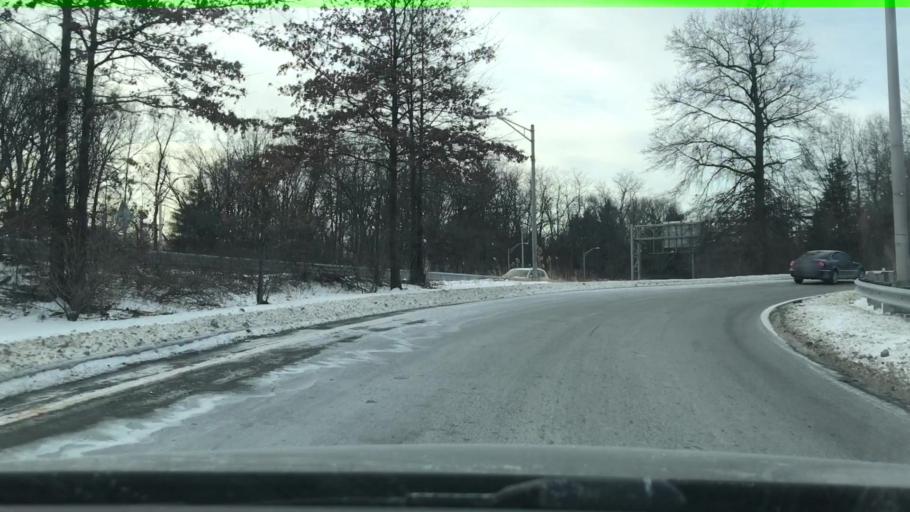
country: US
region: New Jersey
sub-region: Morris County
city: Parsippany
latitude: 40.8314
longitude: -74.4376
